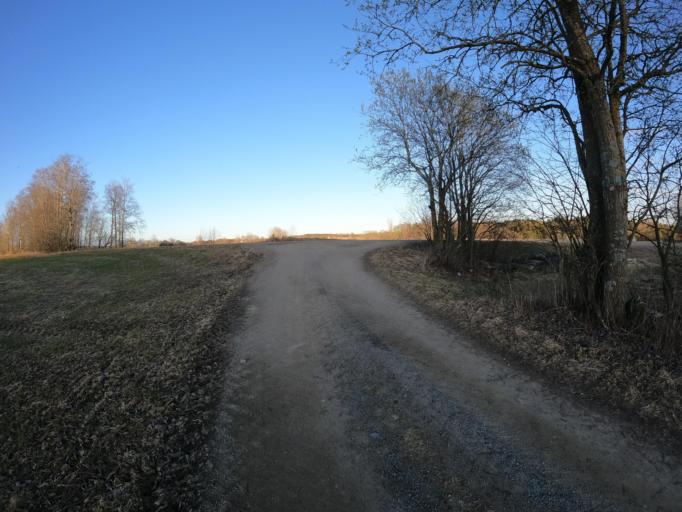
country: NO
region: Akershus
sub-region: Nannestad
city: Teigebyen
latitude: 60.2375
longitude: 10.9877
